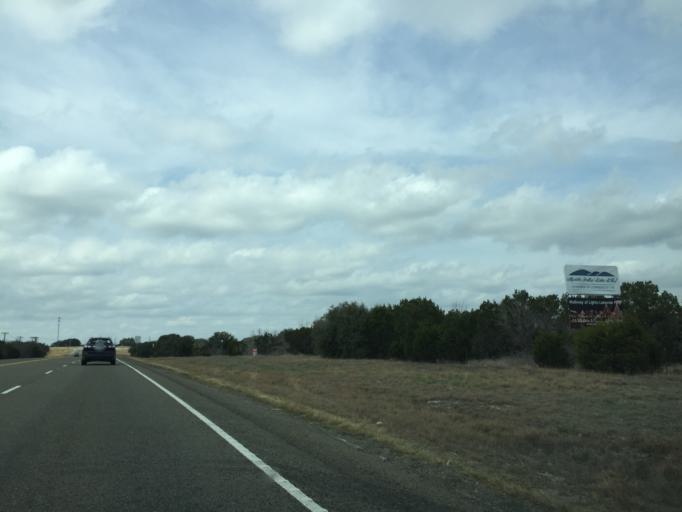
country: US
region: Texas
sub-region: Burnet County
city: Meadowlakes
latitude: 30.5072
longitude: -98.2879
